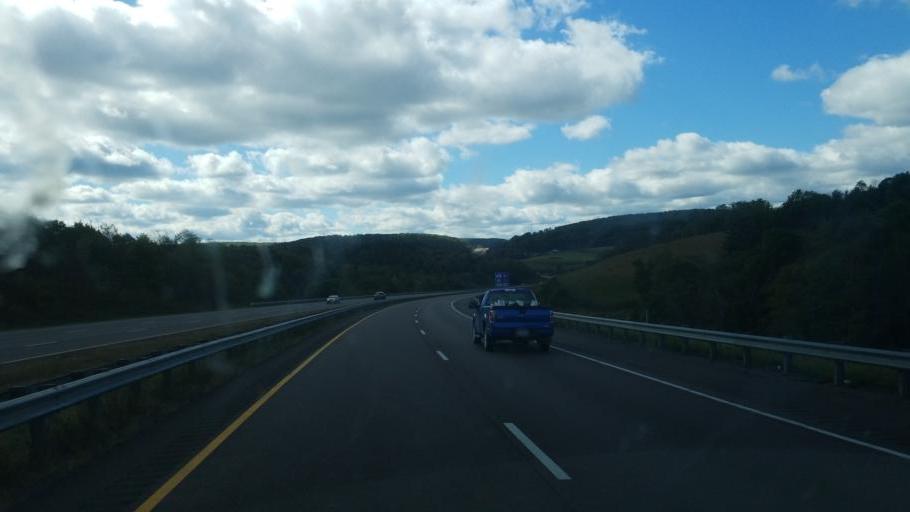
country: US
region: Maryland
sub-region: Allegany County
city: Frostburg
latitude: 39.6820
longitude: -79.0432
